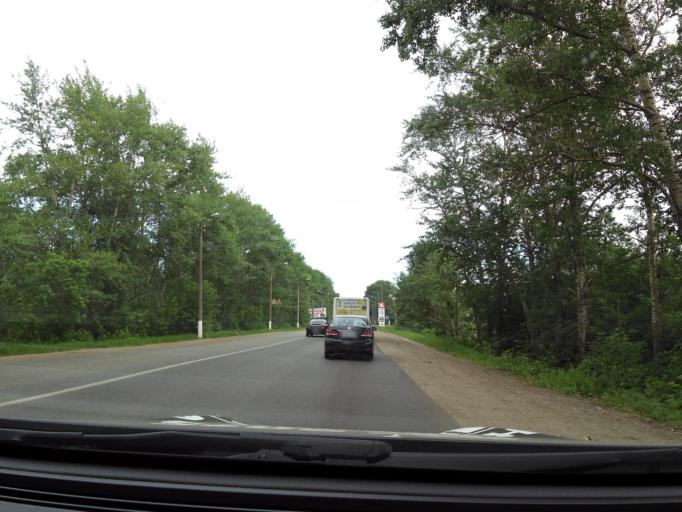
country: RU
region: Kirov
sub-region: Kirovo-Chepetskiy Rayon
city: Kirov
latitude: 58.6186
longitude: 49.7110
